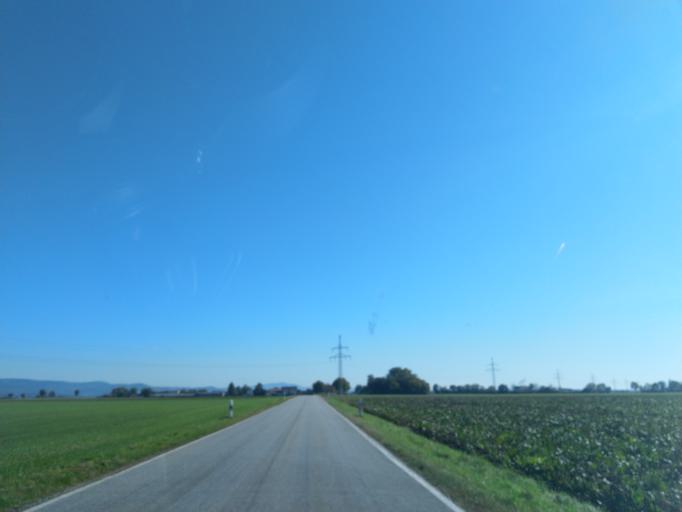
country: DE
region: Bavaria
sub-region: Lower Bavaria
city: Stephansposching
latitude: 48.7941
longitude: 12.7910
